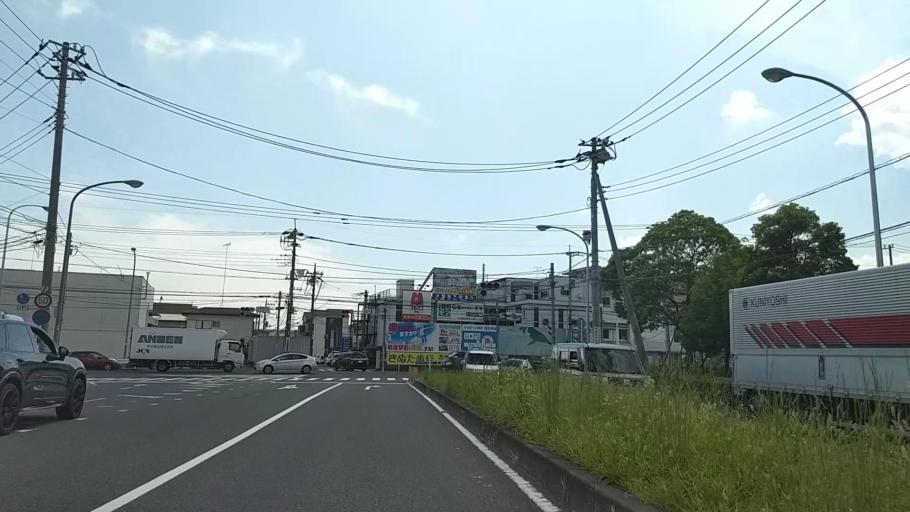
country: JP
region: Kanagawa
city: Yokohama
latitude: 35.5167
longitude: 139.5686
